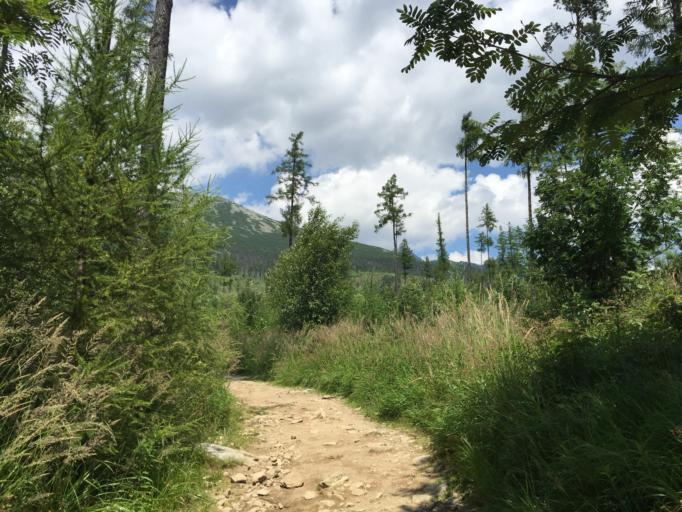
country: SK
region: Presovsky
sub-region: Okres Poprad
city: Vysoke Tatry
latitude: 49.1460
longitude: 20.2168
